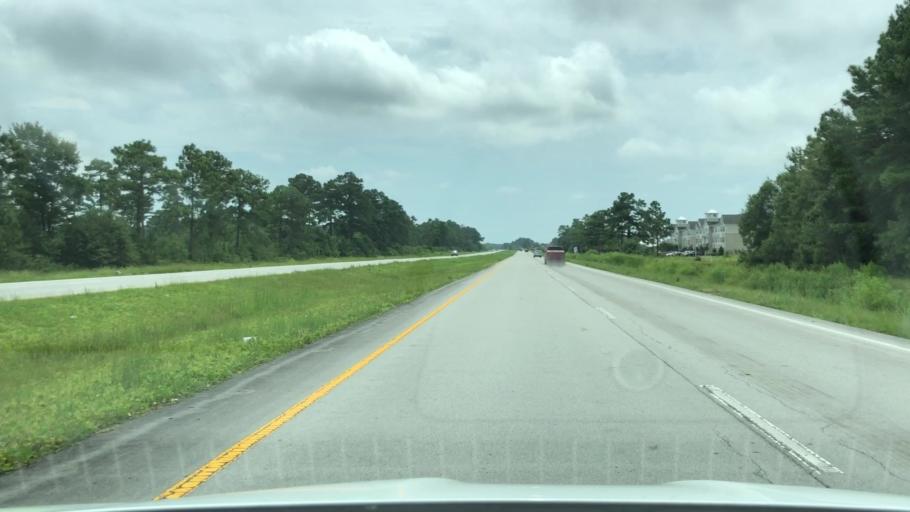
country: US
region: North Carolina
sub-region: Carteret County
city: Newport
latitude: 34.8000
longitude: -76.8783
